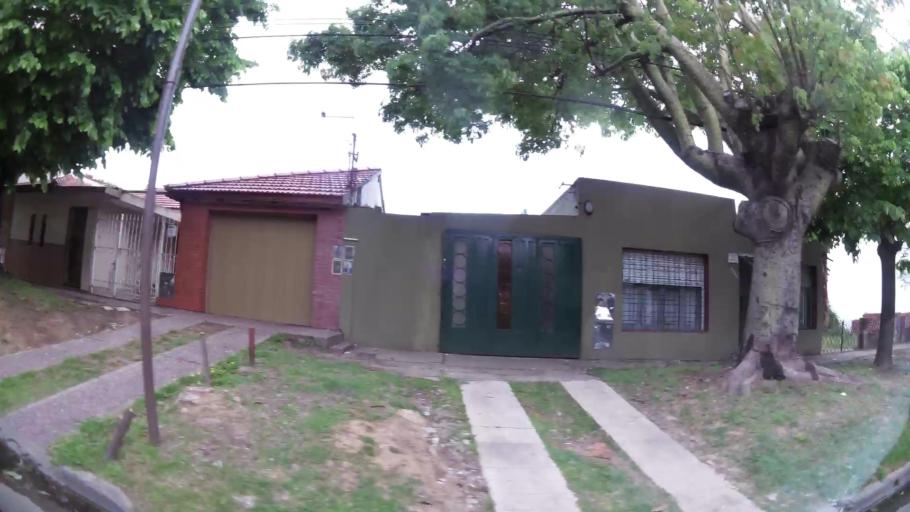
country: AR
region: Buenos Aires
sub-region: Partido de Quilmes
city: Quilmes
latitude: -34.7662
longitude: -58.2770
